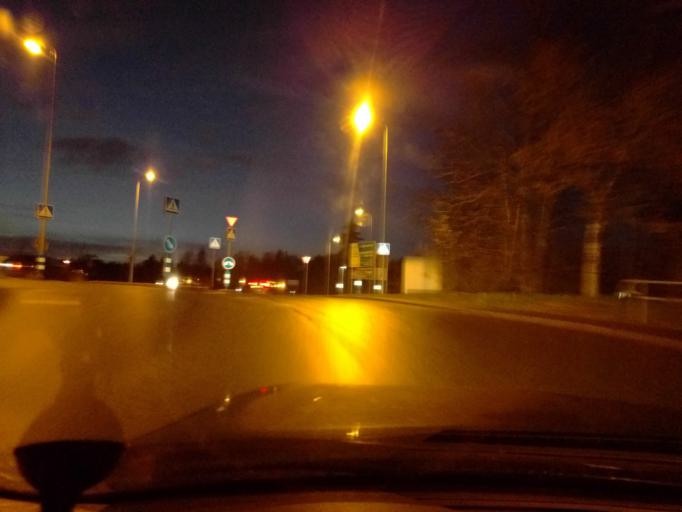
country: EE
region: Harju
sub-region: Tallinna linn
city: Tallinn
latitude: 59.3687
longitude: 24.7182
